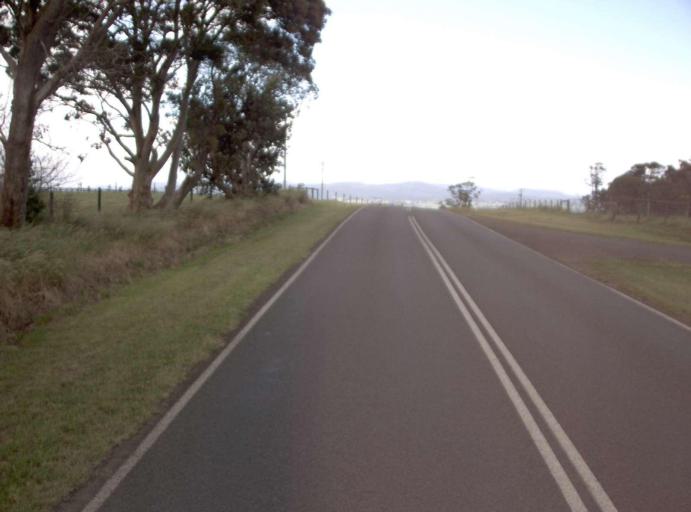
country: AU
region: Victoria
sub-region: Baw Baw
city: Warragul
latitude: -38.1158
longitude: 145.9259
